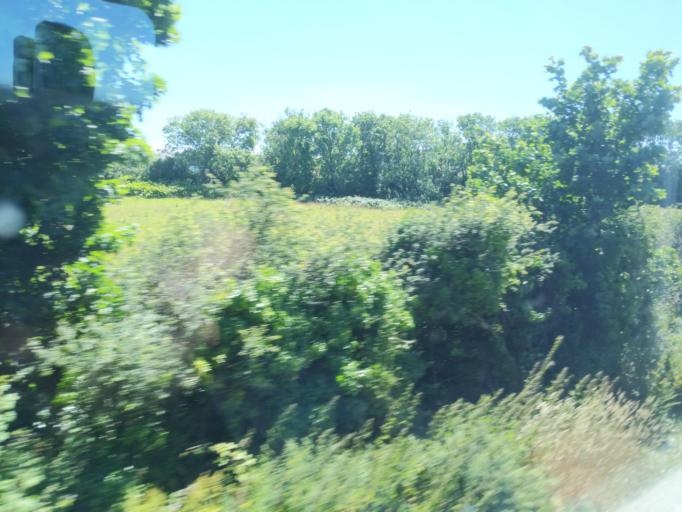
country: GB
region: England
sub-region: Cornwall
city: Redruth
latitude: 50.2484
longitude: -5.2148
